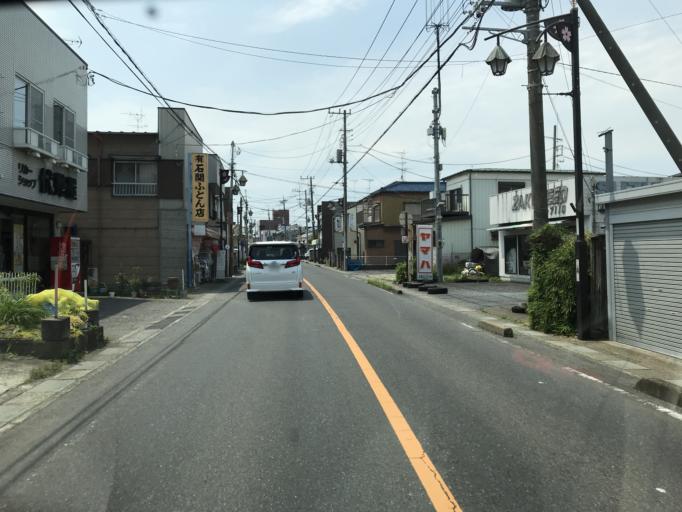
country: JP
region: Saitama
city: Satte
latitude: 36.0798
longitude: 139.7221
